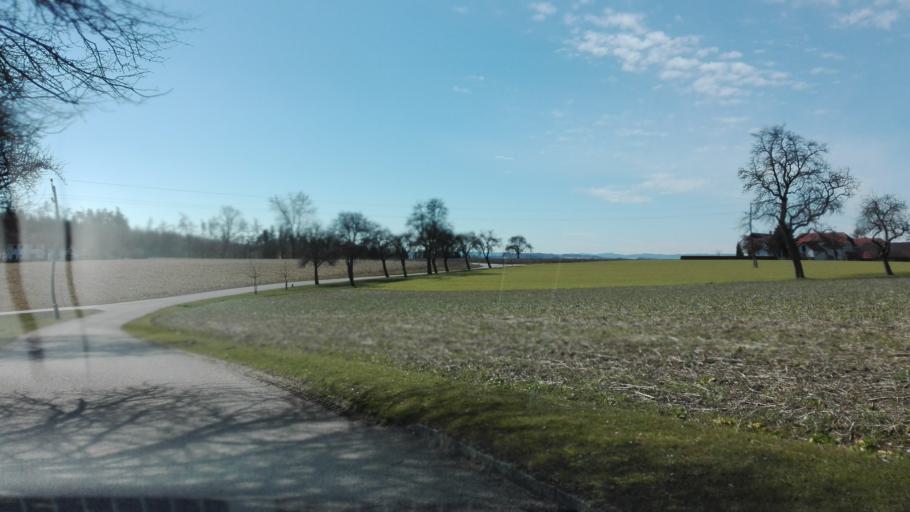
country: AT
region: Upper Austria
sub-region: Politischer Bezirk Grieskirchen
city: Grieskirchen
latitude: 48.2359
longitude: 13.8562
